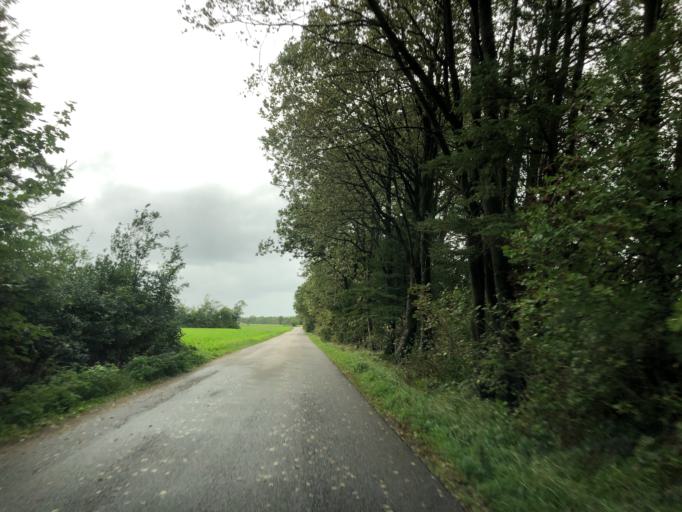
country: DK
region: Central Jutland
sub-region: Holstebro Kommune
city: Holstebro
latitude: 56.2330
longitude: 8.5294
